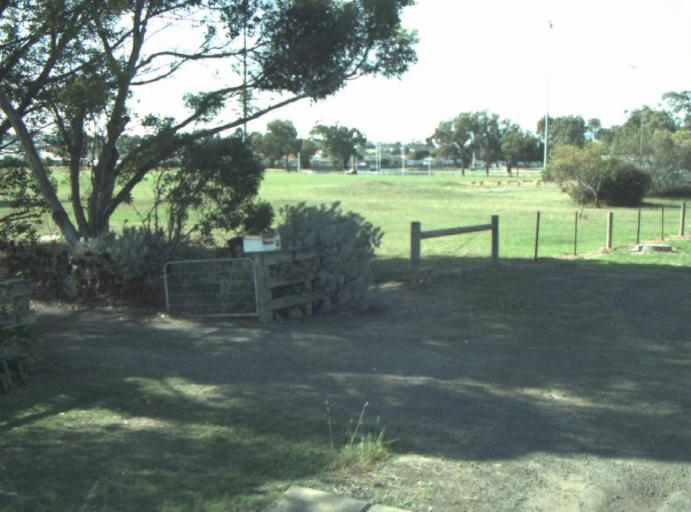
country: AU
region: Victoria
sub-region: Greater Geelong
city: Leopold
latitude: -38.1825
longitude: 144.4564
